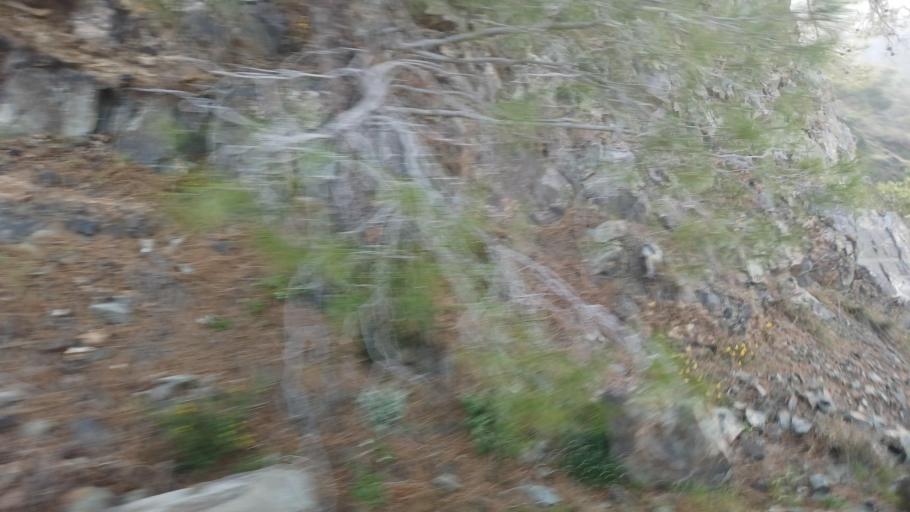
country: CY
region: Pafos
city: Polis
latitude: 35.0020
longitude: 32.3353
